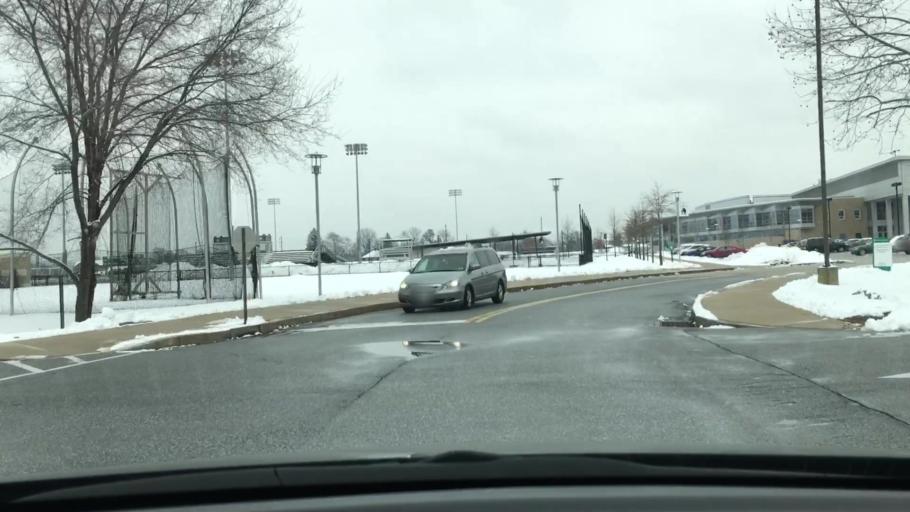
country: US
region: Pennsylvania
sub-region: York County
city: Grantley
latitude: 39.9448
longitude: -76.7389
